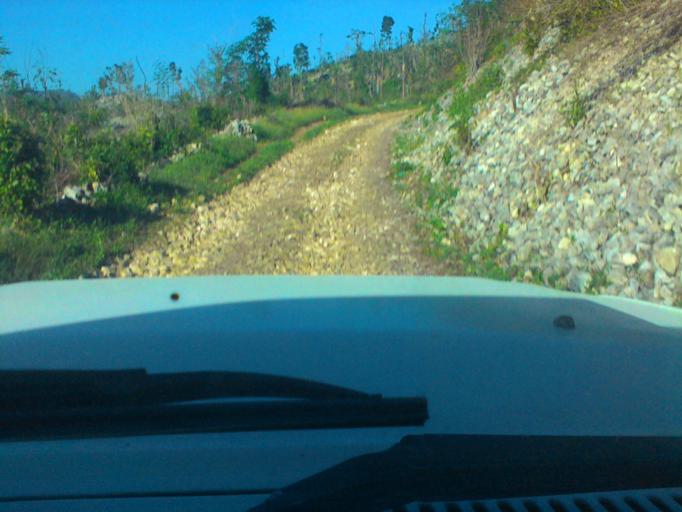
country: HT
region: Grandans
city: Jeremie
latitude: 18.5198
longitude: -74.0789
